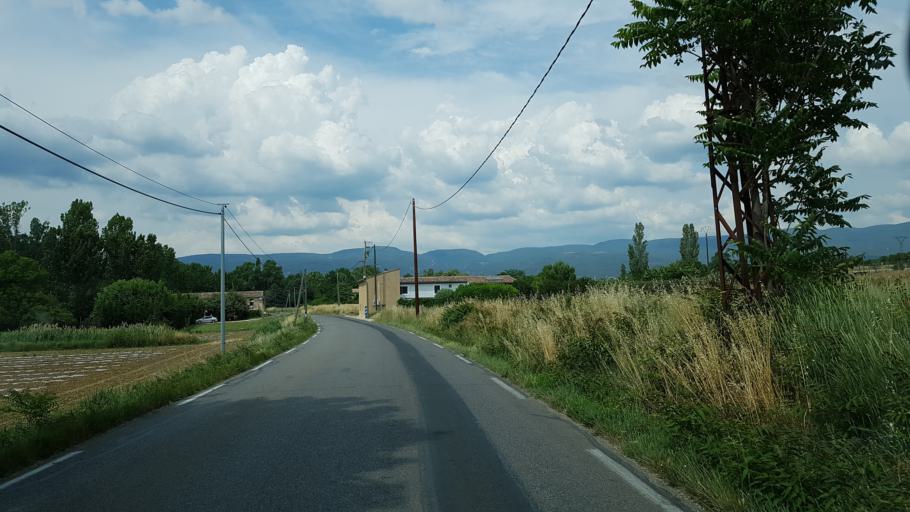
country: FR
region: Provence-Alpes-Cote d'Azur
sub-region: Departement du Vaucluse
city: Apt
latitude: 43.8958
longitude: 5.3831
